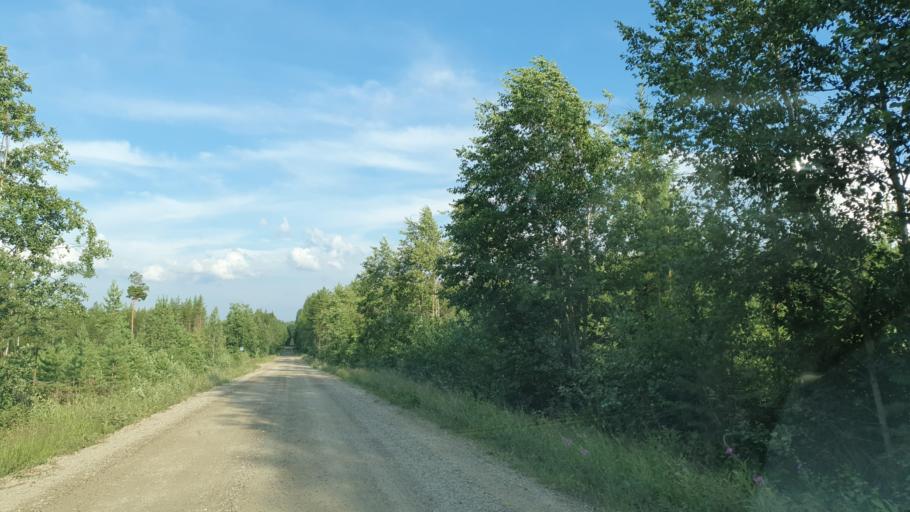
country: FI
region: Kainuu
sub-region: Kehys-Kainuu
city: Kuhmo
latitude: 64.2754
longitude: 29.7973
